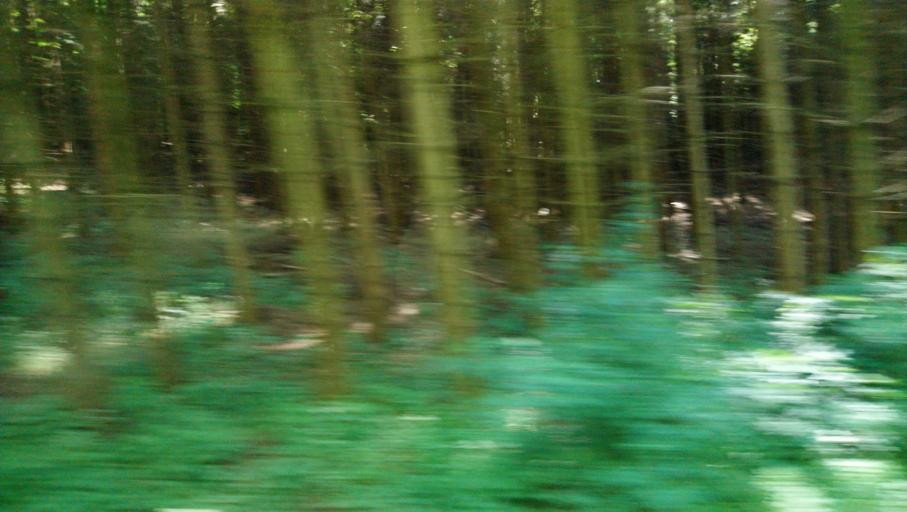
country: LU
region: Diekirch
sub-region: Canton de Vianden
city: Tandel
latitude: 49.9056
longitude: 6.1876
